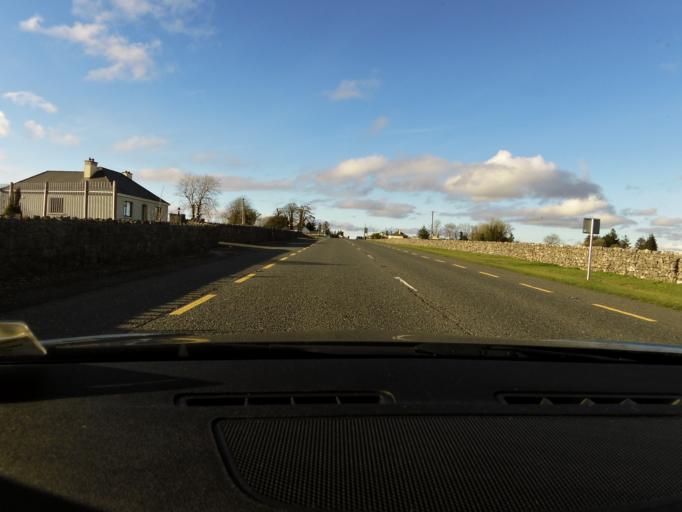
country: IE
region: Connaught
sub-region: Roscommon
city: Roscommon
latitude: 53.6622
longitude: -8.1981
